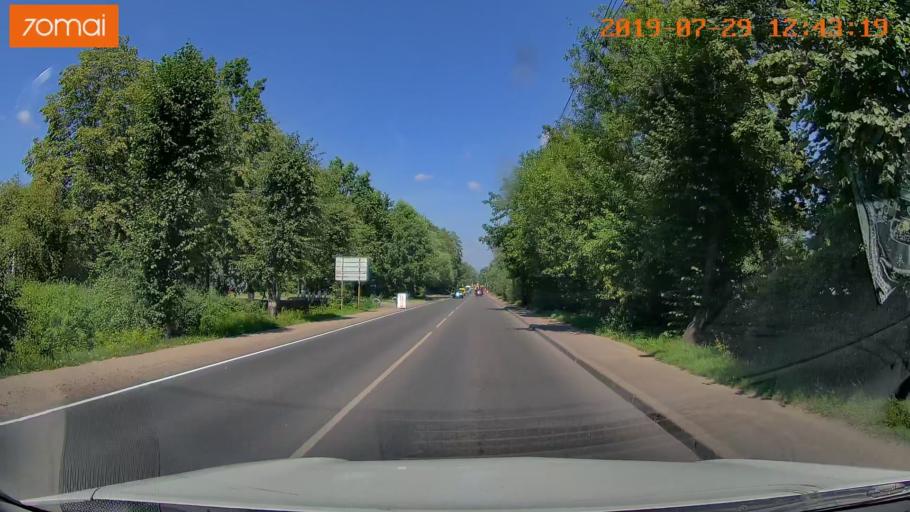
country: RU
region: Kaliningrad
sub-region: Gorod Kaliningrad
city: Kaliningrad
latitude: 54.6754
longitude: 20.5414
